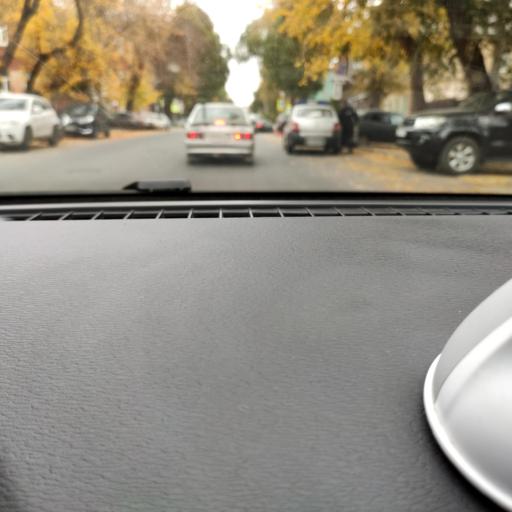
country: RU
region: Samara
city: Samara
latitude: 53.1809
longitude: 50.0922
